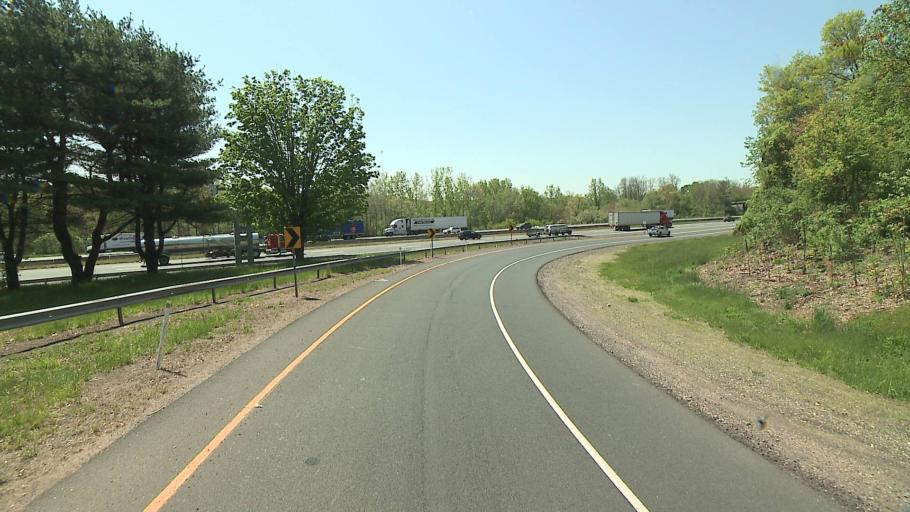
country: US
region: Connecticut
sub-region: Tolland County
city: Rockville
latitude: 41.8343
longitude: -72.4646
